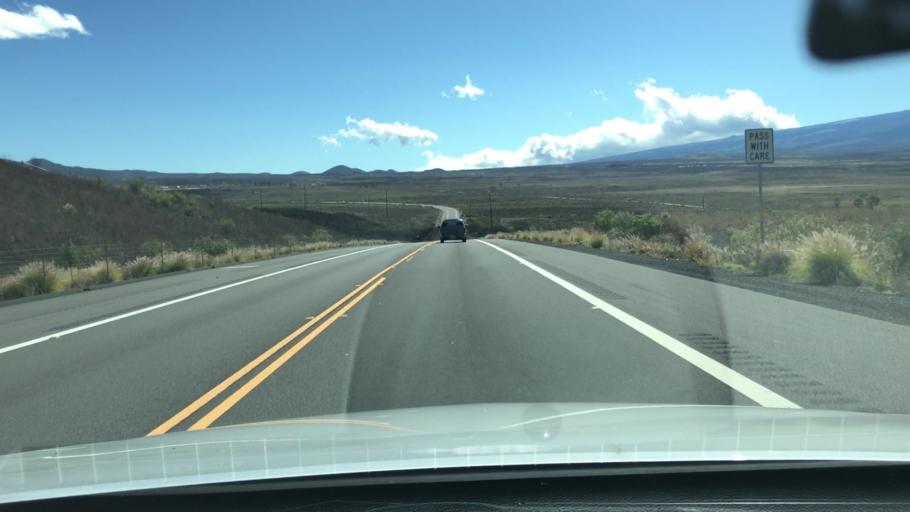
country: US
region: Hawaii
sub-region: Hawaii County
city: Waikoloa
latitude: 19.7739
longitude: -155.5909
